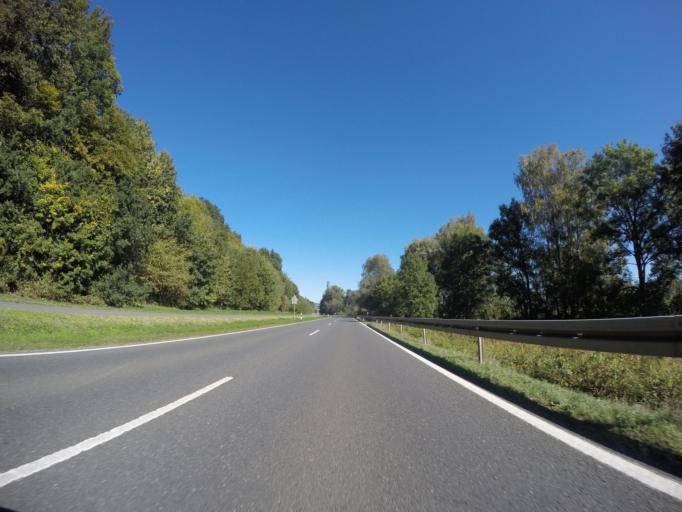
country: DE
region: Bavaria
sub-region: Upper Franconia
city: Wiesenthau
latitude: 49.7279
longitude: 11.1249
